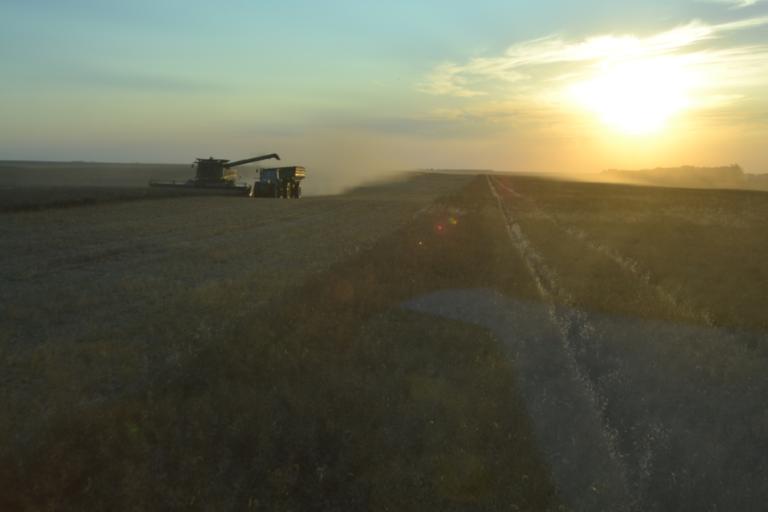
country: US
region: North Dakota
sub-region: Mercer County
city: Beulah
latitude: 47.7013
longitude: -101.9730
